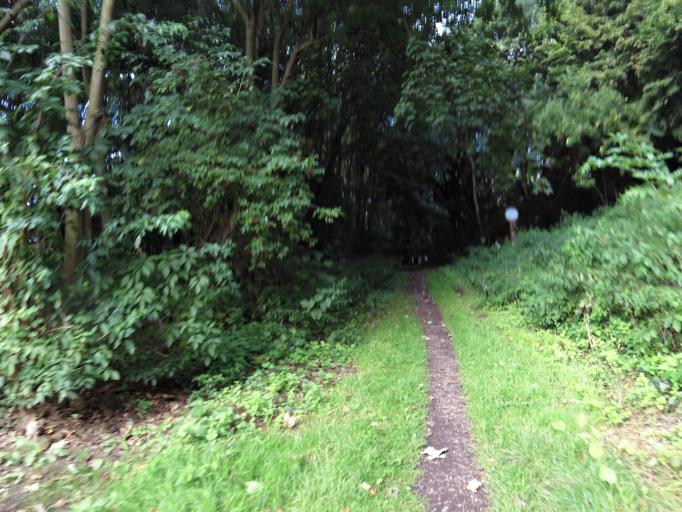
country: DE
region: North Rhine-Westphalia
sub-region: Regierungsbezirk Koln
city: Alsdorf
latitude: 50.8541
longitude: 6.1852
